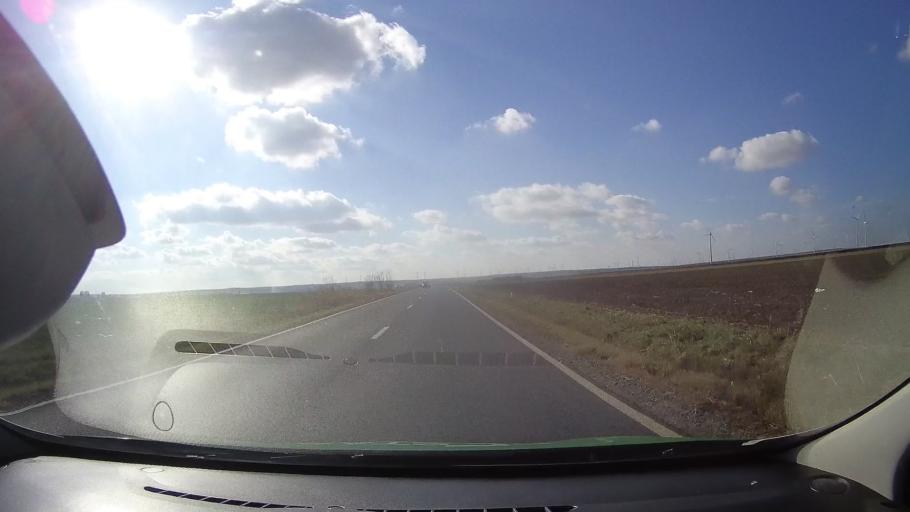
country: RO
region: Constanta
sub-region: Comuna Mihai Viteazu
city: Mihai Viteazu
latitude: 44.6643
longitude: 28.6797
